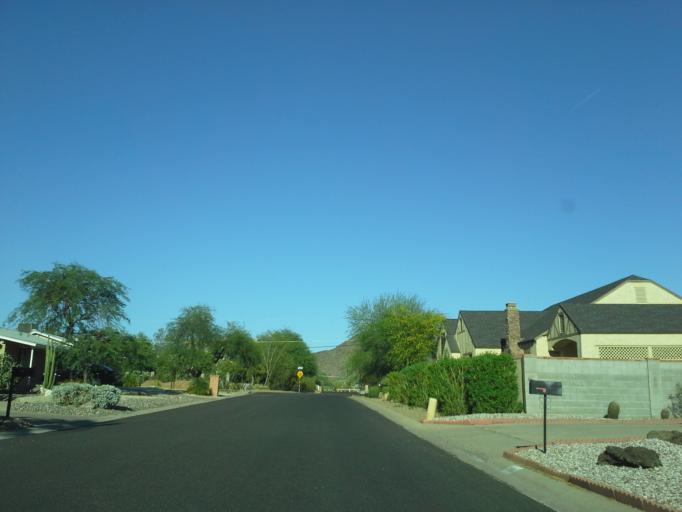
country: US
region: Arizona
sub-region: Maricopa County
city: Paradise Valley
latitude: 33.5579
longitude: -112.0488
